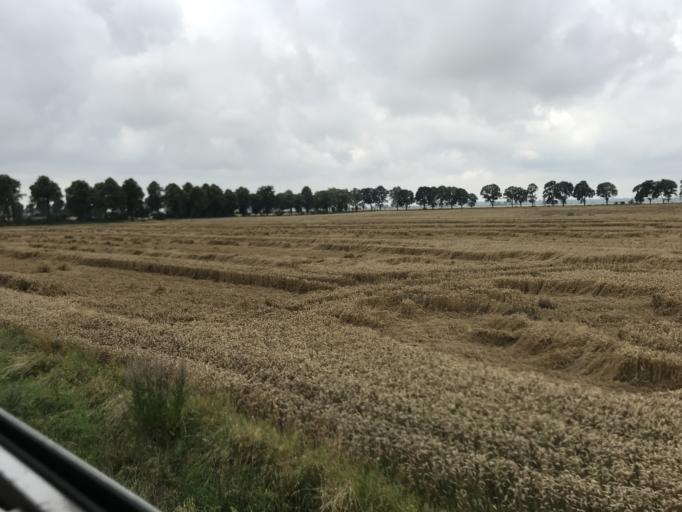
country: PL
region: Pomeranian Voivodeship
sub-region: Powiat malborski
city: Stare Pole
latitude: 54.0610
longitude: 19.2321
